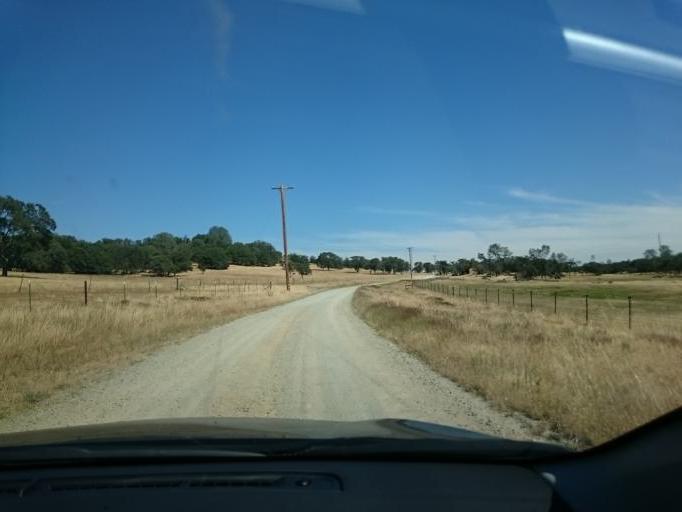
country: US
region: California
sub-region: Calaveras County
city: Rancho Calaveras
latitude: 38.0775
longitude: -120.7425
